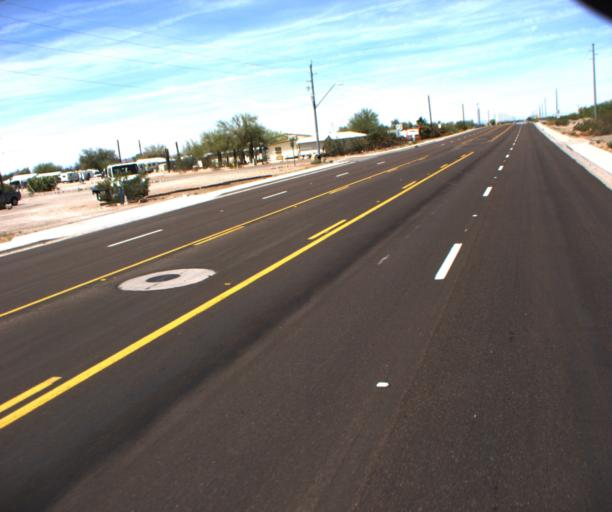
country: US
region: Arizona
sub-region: La Paz County
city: Quartzsite
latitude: 33.6840
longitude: -114.2170
